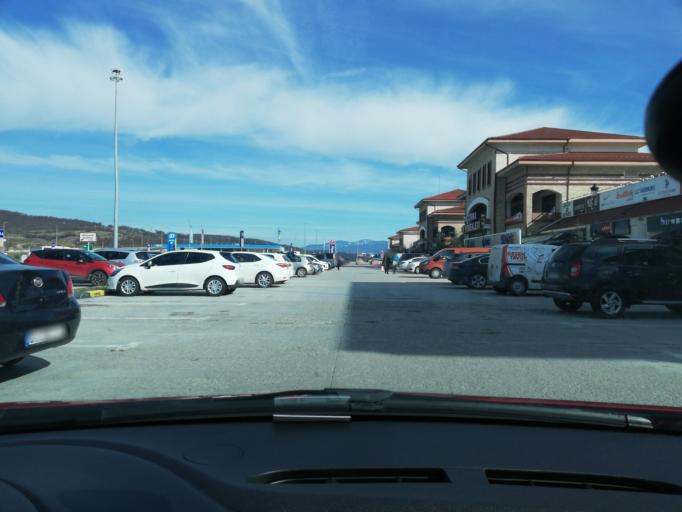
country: TR
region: Bolu
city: Bolu
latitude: 40.7231
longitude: 31.4651
